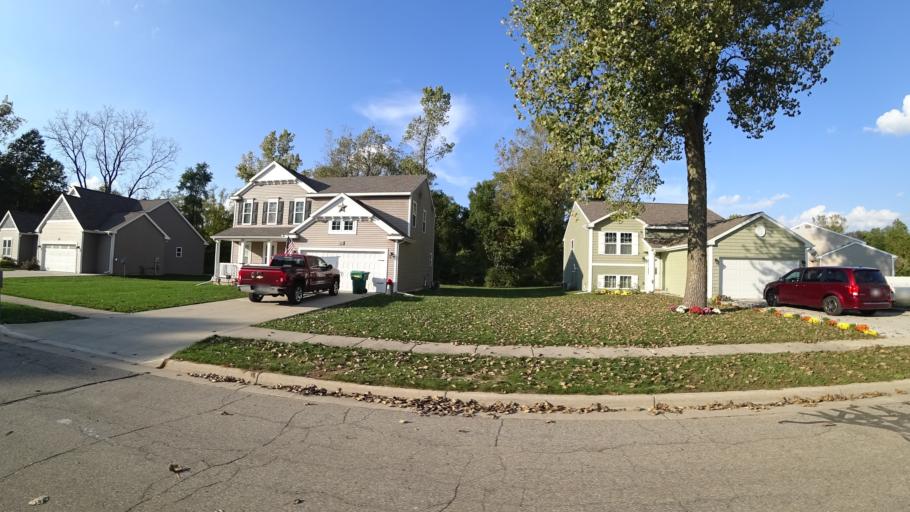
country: US
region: Michigan
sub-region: Saint Joseph County
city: Three Rivers
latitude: 41.9600
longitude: -85.6262
